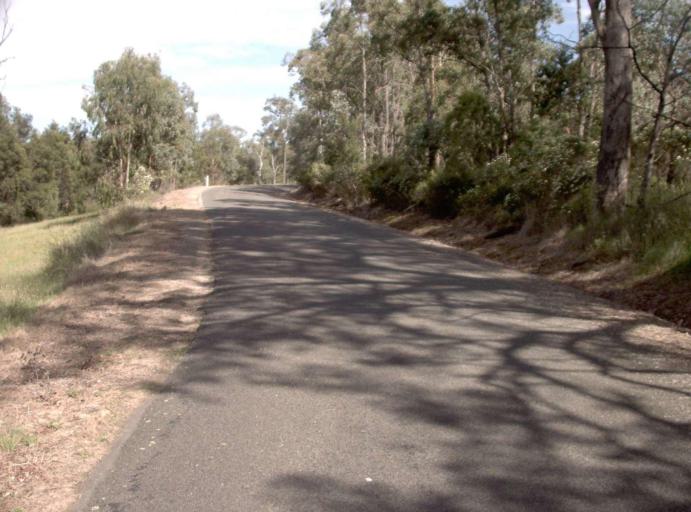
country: AU
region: Victoria
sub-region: East Gippsland
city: Lakes Entrance
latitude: -37.4878
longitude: 148.1296
